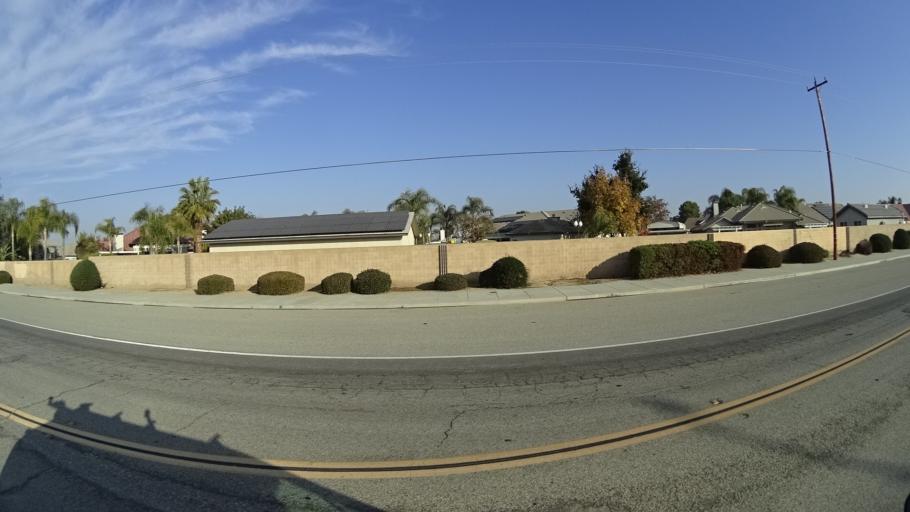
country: US
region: California
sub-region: Kern County
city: Rosedale
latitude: 35.3835
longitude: -119.1706
